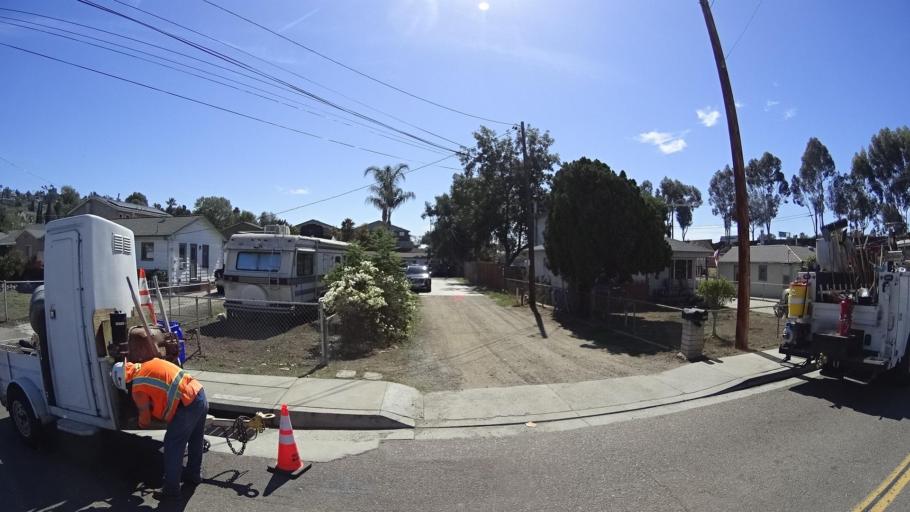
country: US
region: California
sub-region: San Diego County
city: Spring Valley
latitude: 32.7277
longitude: -117.0136
